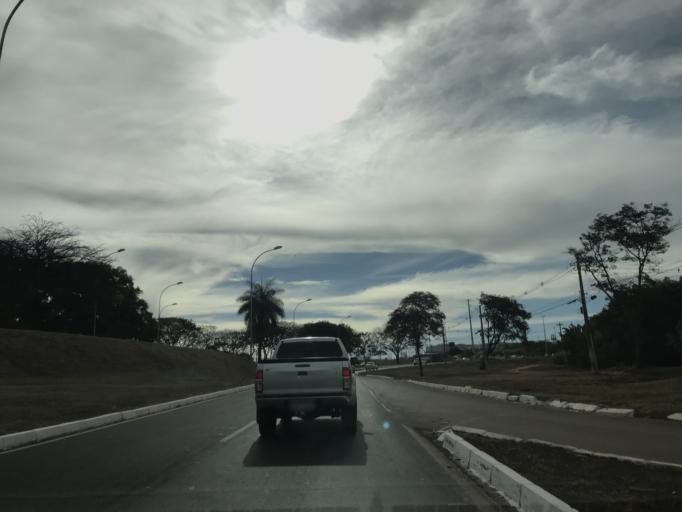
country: BR
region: Federal District
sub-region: Brasilia
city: Brasilia
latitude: -15.8399
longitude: -47.9516
